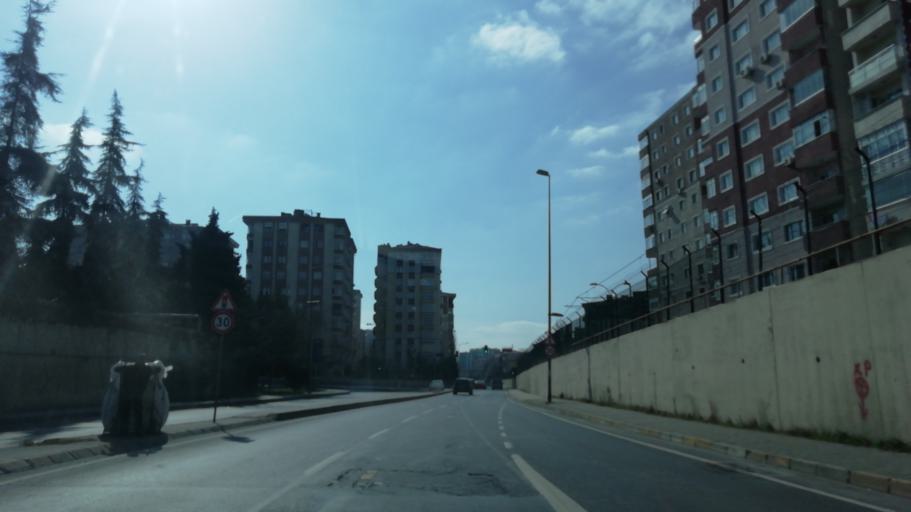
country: TR
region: Istanbul
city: merter keresteciler
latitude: 41.0182
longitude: 28.9009
